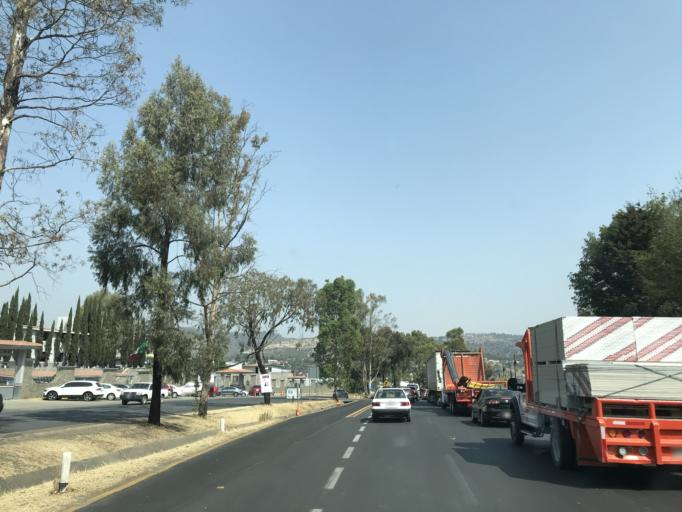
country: MX
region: Tlaxcala
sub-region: Apetatitlan de Antonio Carvajal
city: Tlatempan
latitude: 19.3359
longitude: -98.1984
